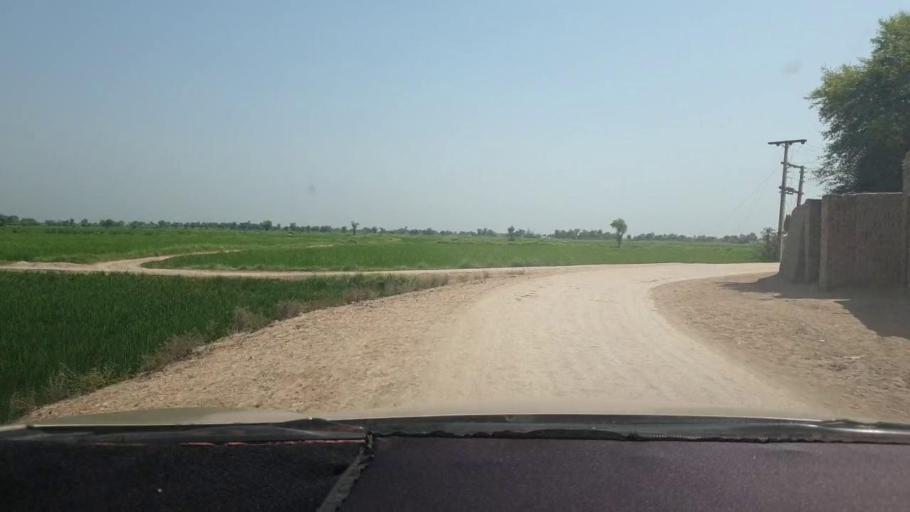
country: PK
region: Sindh
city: Miro Khan
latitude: 27.6696
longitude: 68.0993
